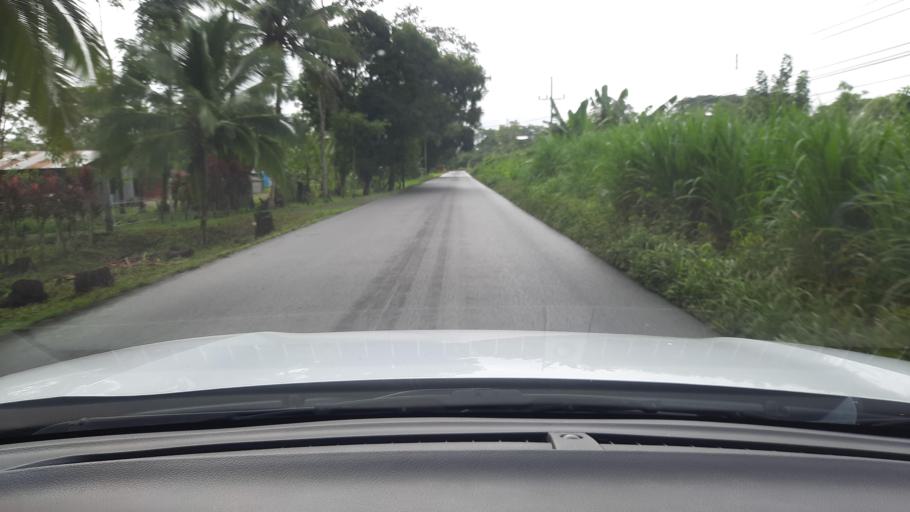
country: CR
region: Alajuela
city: Upala
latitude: 10.9254
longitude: -85.0736
